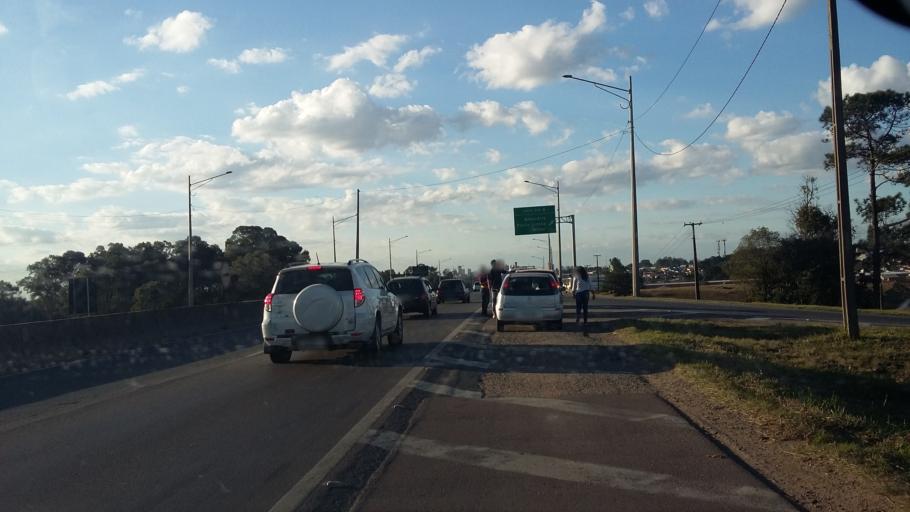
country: BR
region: Parana
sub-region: Sao Jose Dos Pinhais
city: Sao Jose dos Pinhais
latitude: -25.5458
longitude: -49.3035
